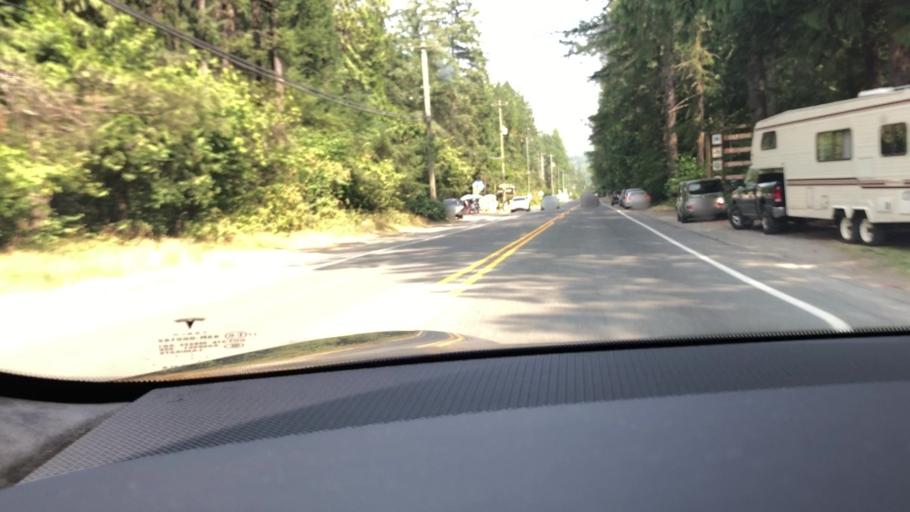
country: CA
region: British Columbia
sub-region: Fraser Valley Regional District
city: Chilliwack
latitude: 49.0749
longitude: -121.9732
